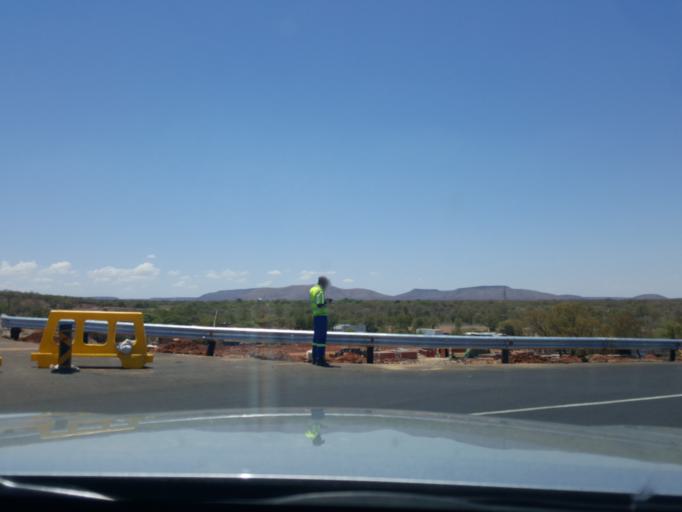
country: BW
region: South East
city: Ramotswa
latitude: -24.8283
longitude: 25.8072
